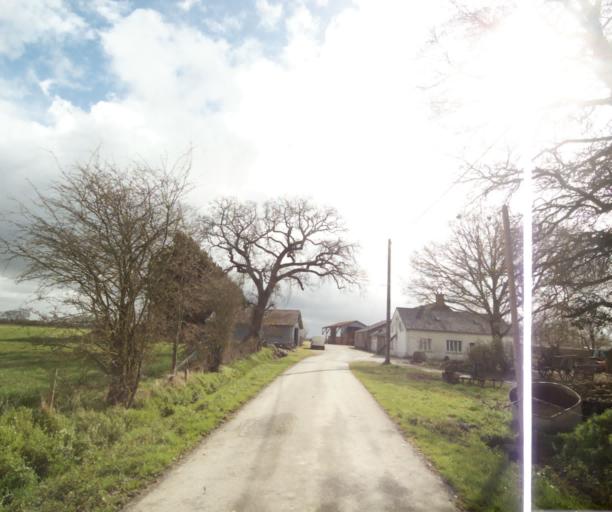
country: FR
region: Pays de la Loire
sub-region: Departement de la Loire-Atlantique
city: Bouvron
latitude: 47.4480
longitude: -1.8957
